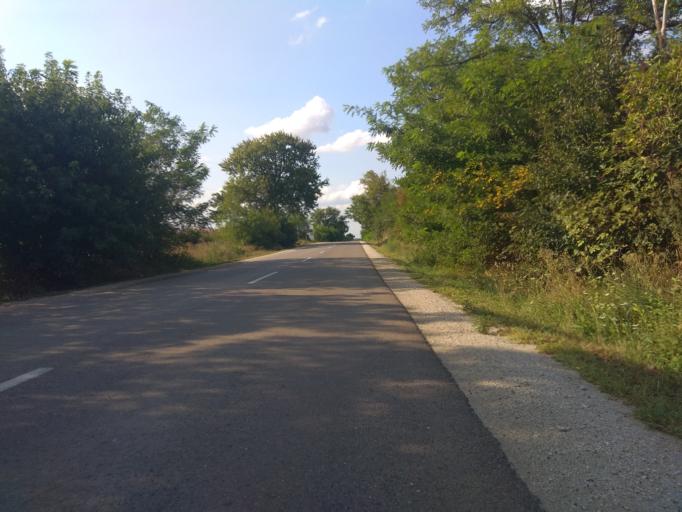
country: HU
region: Borsod-Abauj-Zemplen
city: Hejobaba
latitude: 47.8974
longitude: 20.8919
